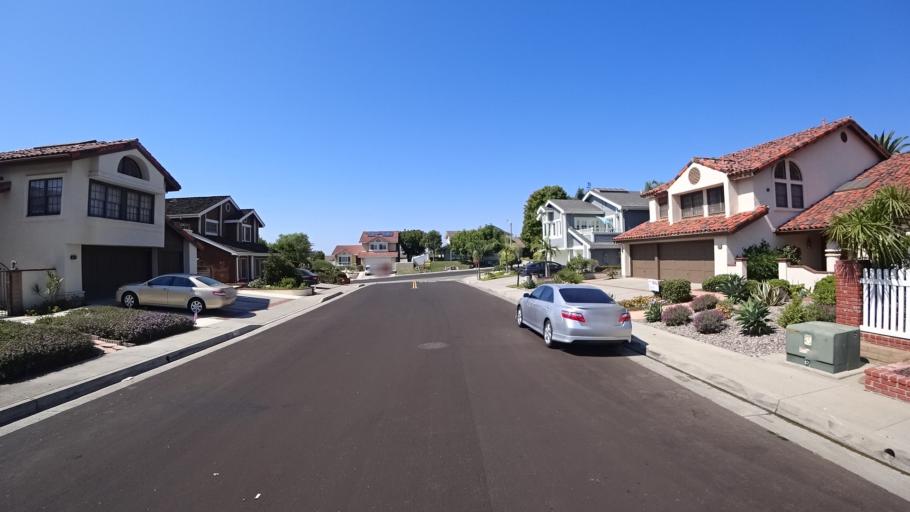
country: US
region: California
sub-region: Orange County
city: San Clemente
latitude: 33.4504
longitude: -117.6368
